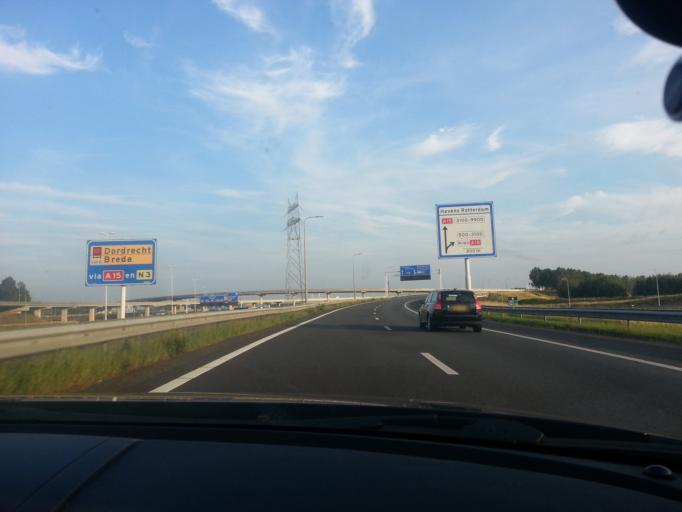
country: NL
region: South Holland
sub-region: Gemeente Capelle aan den IJssel
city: Capelle-West
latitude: 51.8795
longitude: 4.5662
